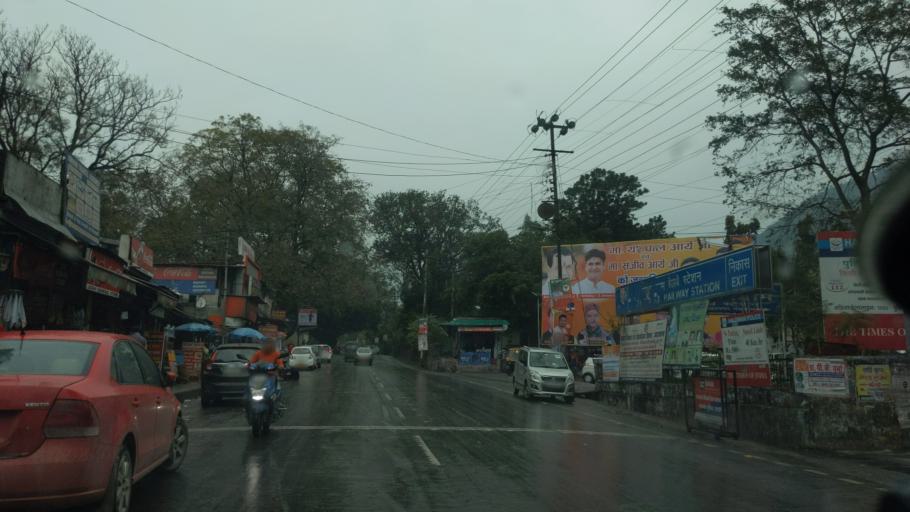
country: IN
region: Uttarakhand
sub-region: Naini Tal
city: Haldwani
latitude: 29.2652
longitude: 79.5446
